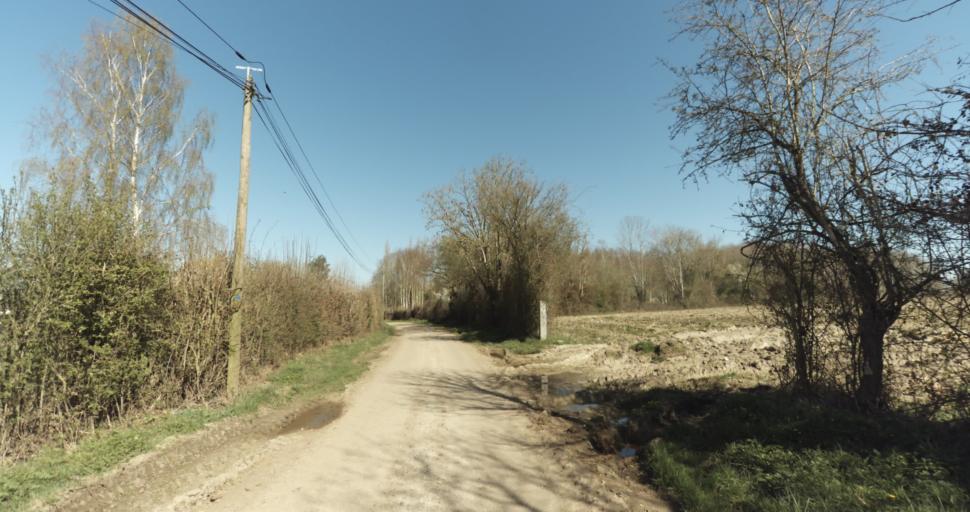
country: FR
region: Lower Normandy
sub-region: Departement du Calvados
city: Livarot
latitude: 49.0167
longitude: 0.1044
